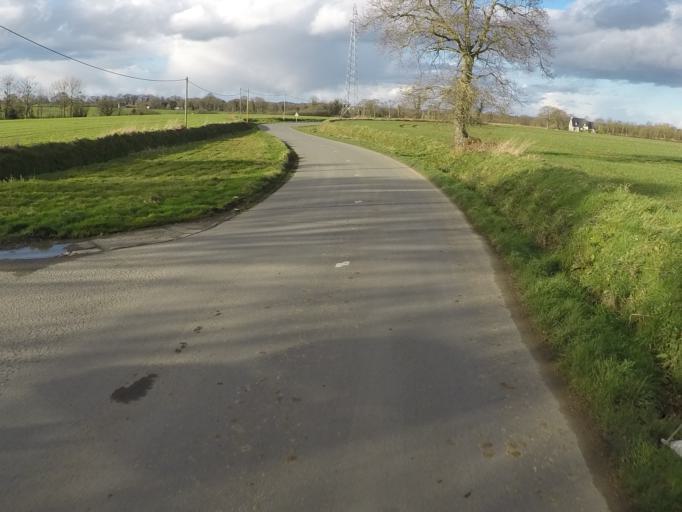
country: FR
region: Brittany
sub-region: Departement des Cotes-d'Armor
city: Plelo
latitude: 48.5631
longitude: -2.9786
